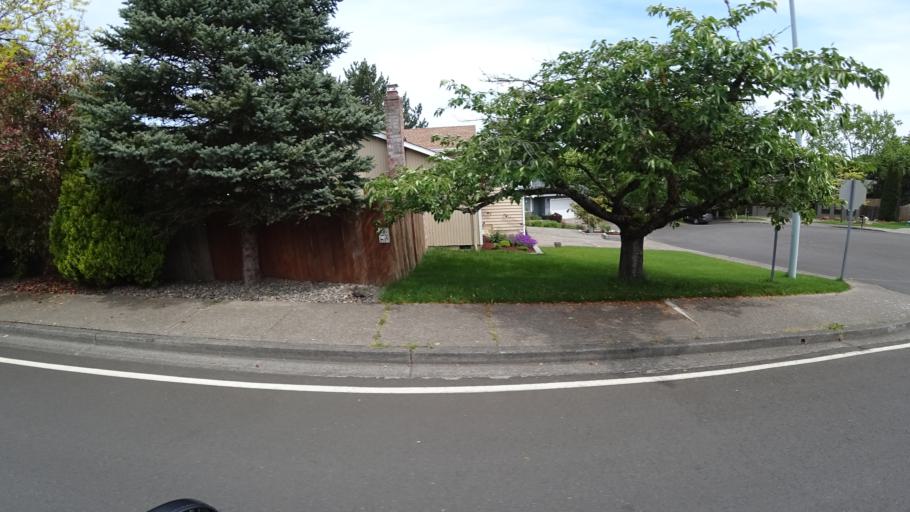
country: US
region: Oregon
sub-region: Washington County
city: Aloha
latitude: 45.4601
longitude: -122.8481
